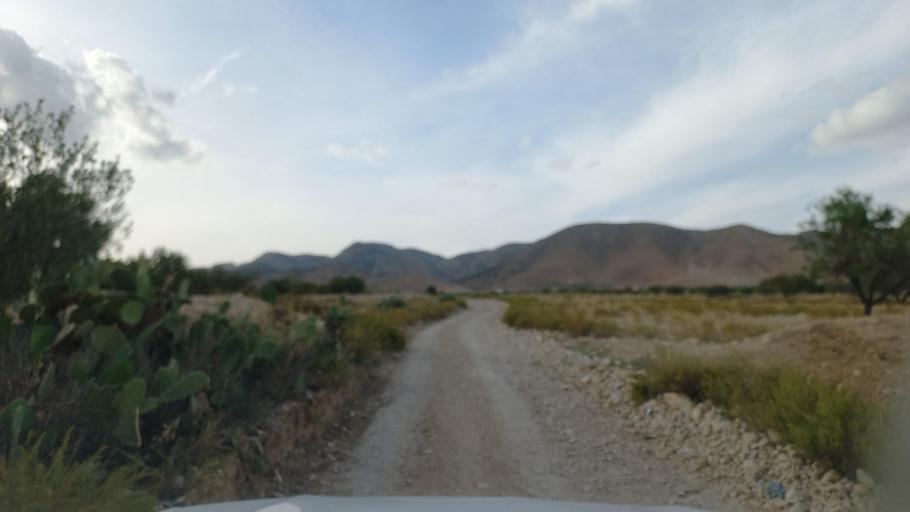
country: TN
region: Al Qasrayn
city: Sbiba
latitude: 35.4441
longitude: 9.0711
